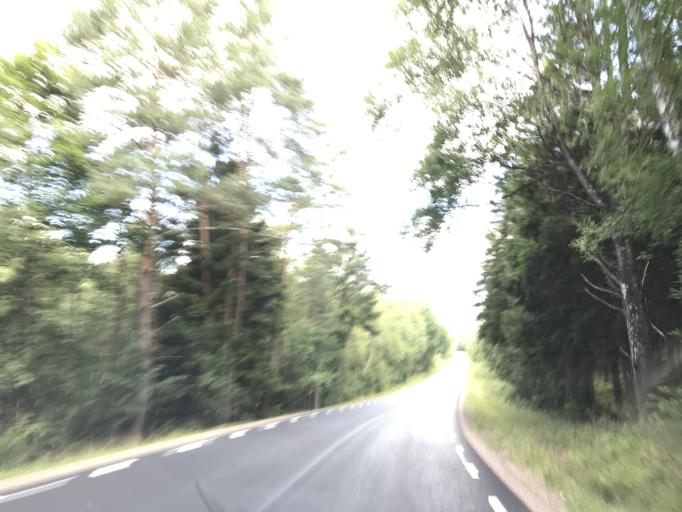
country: SE
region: Halland
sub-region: Laholms Kommun
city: Knared
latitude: 56.4872
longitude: 13.3226
